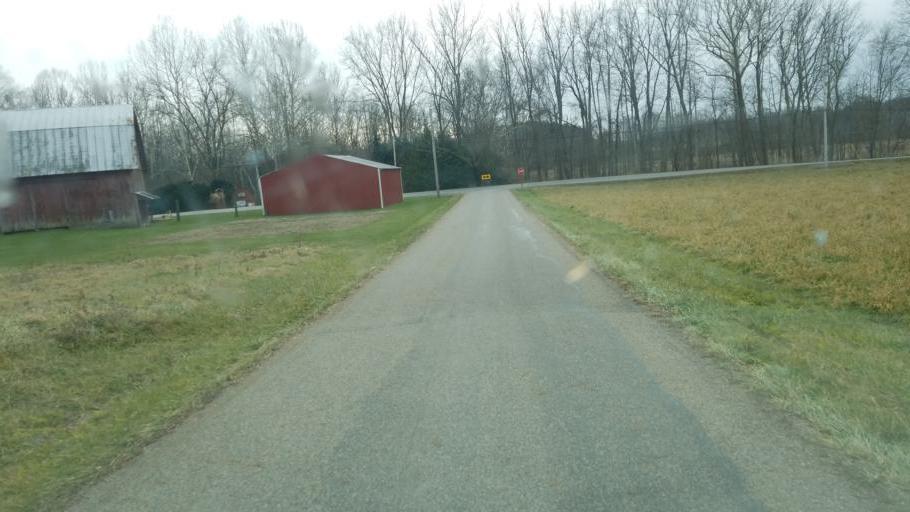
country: US
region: Ohio
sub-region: Richland County
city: Lexington
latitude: 40.6191
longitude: -82.5778
